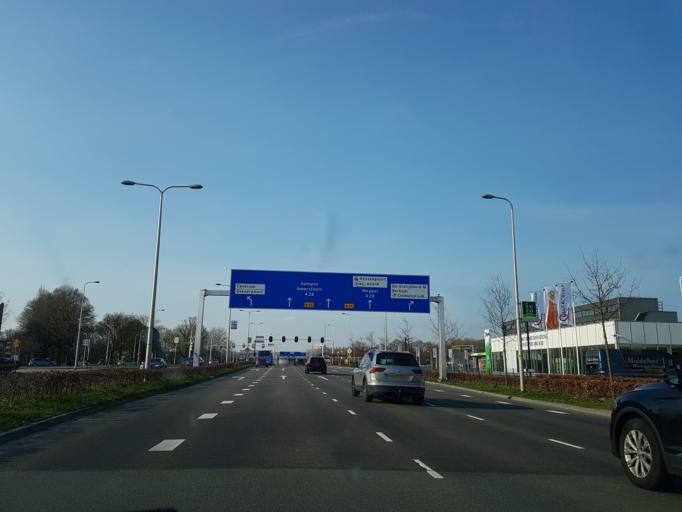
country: NL
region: Overijssel
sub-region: Gemeente Zwolle
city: Zwolle
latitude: 52.5223
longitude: 6.1175
